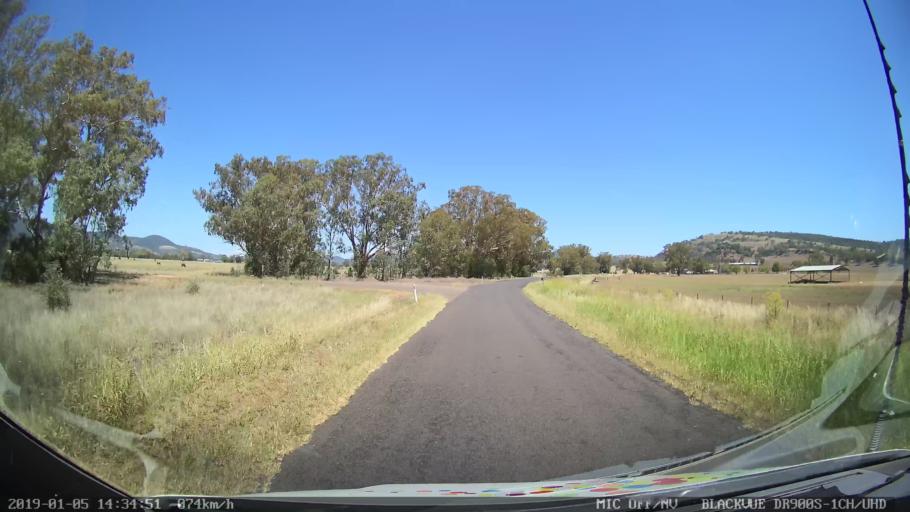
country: AU
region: New South Wales
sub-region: Tamworth Municipality
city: Phillip
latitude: -31.2361
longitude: 150.6457
